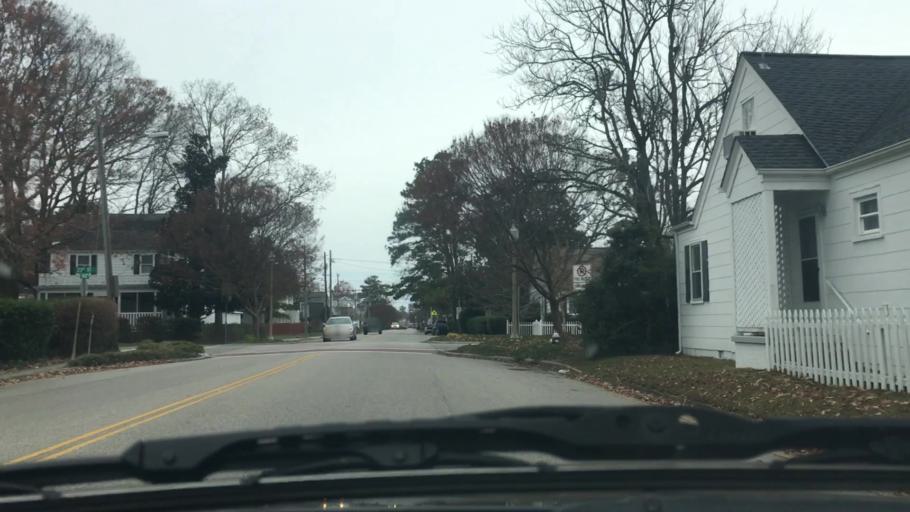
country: US
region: Virginia
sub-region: City of Virginia Beach
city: Virginia Beach
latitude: 36.8501
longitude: -75.9808
